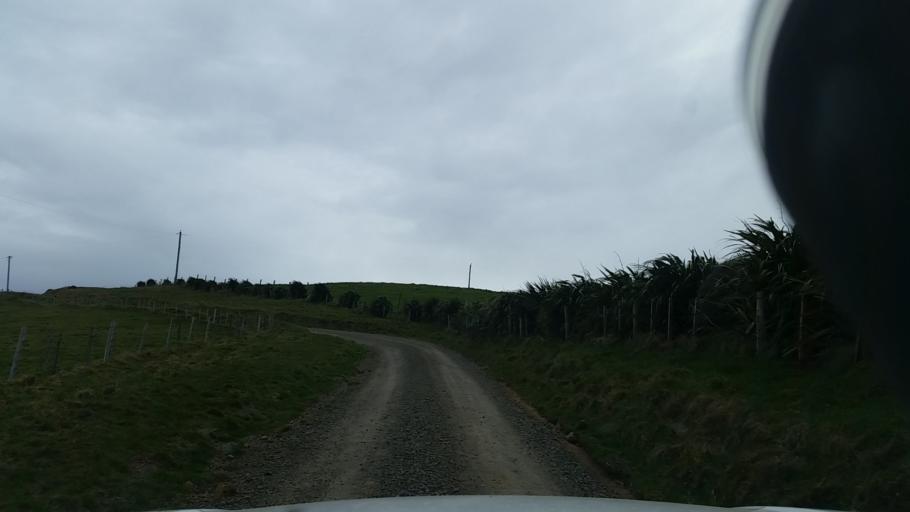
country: NZ
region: Canterbury
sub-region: Christchurch City
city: Christchurch
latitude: -43.8216
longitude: 173.0764
